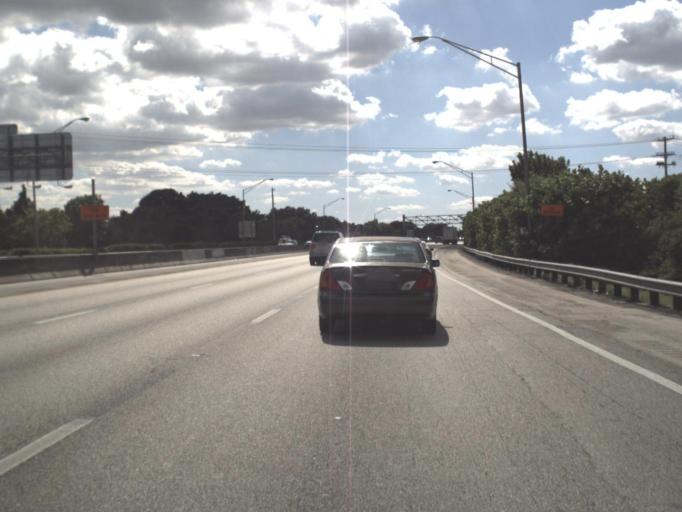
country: US
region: Florida
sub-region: Broward County
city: Pembroke Pines
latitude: 26.0036
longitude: -80.2163
